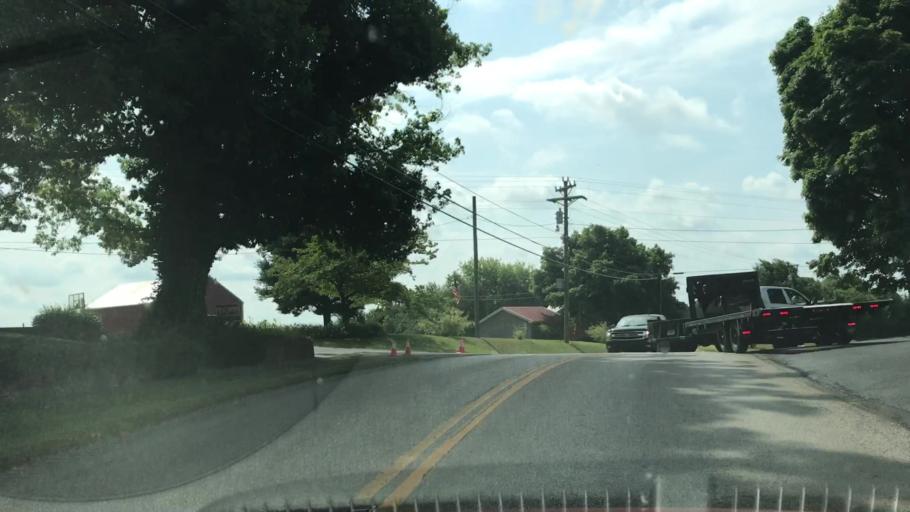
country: US
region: Kentucky
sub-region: Barren County
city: Glasgow
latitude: 36.9756
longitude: -85.8959
